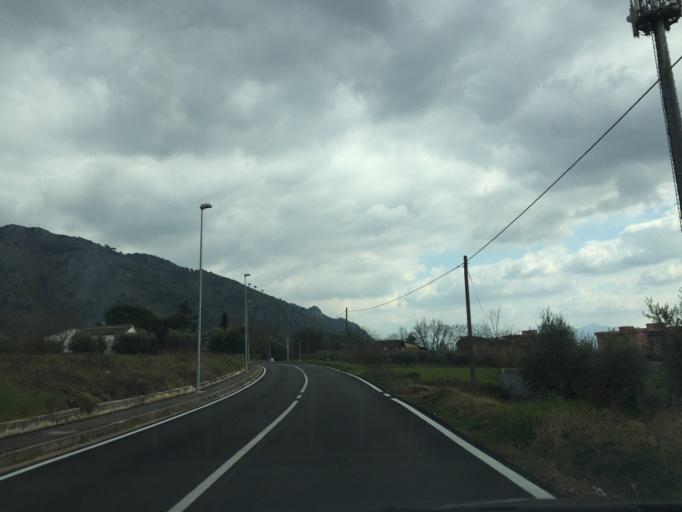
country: IT
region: Latium
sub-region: Provincia di Frosinone
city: Villa Santa Lucia
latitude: 41.4969
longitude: 13.7658
